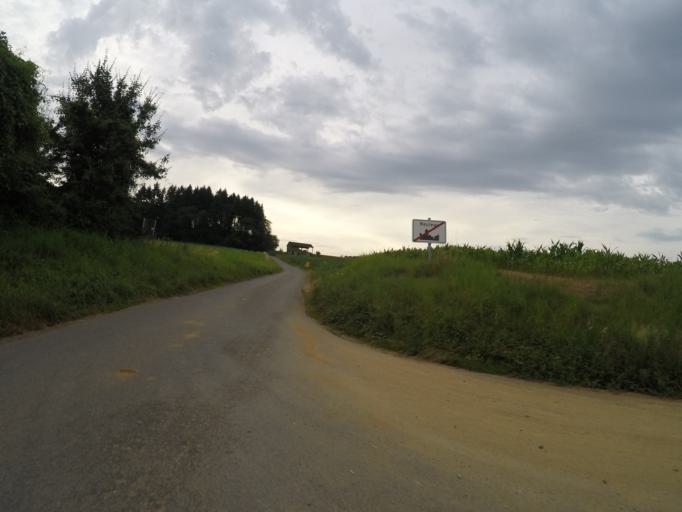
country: BE
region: Wallonia
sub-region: Province de Namur
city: Assesse
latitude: 50.3280
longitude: 5.0370
